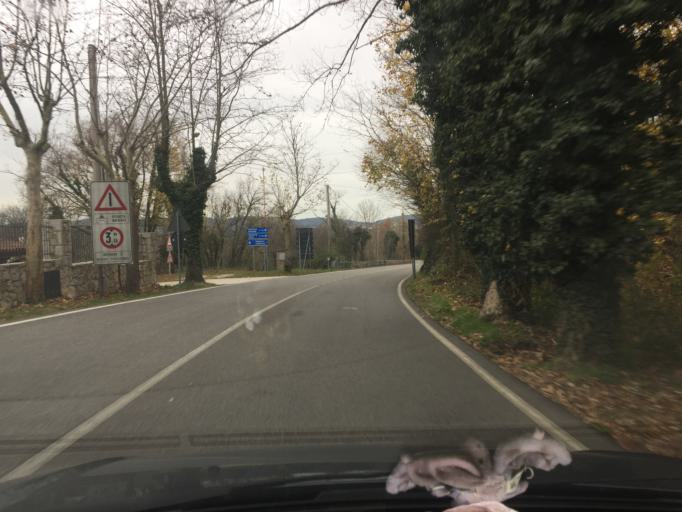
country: IT
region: Friuli Venezia Giulia
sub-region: Provincia di Trieste
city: Zolla
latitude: 45.7129
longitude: 13.8078
